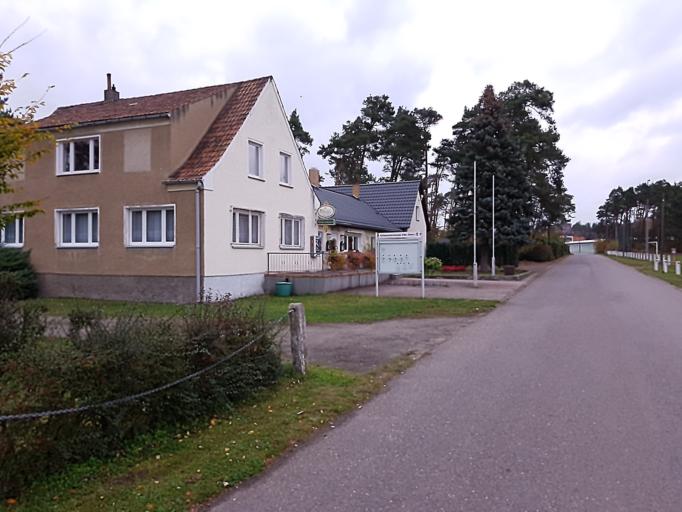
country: DE
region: Brandenburg
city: Schonborn
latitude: 51.5389
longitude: 13.4754
